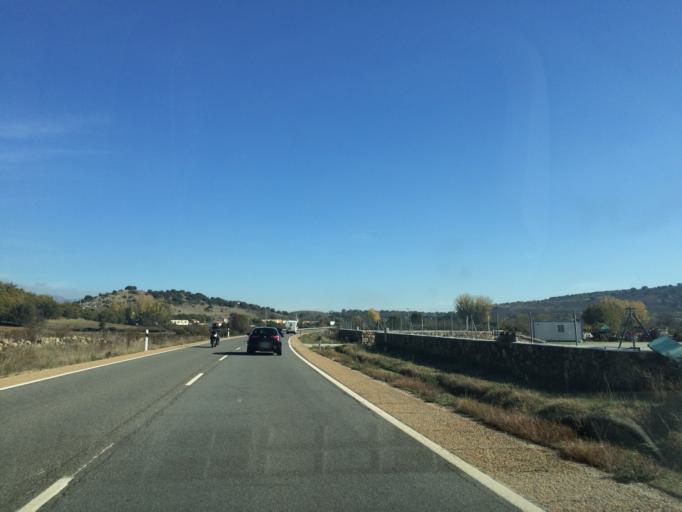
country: ES
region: Madrid
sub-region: Provincia de Madrid
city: Guadalix de la Sierra
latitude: 40.7915
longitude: -3.6972
